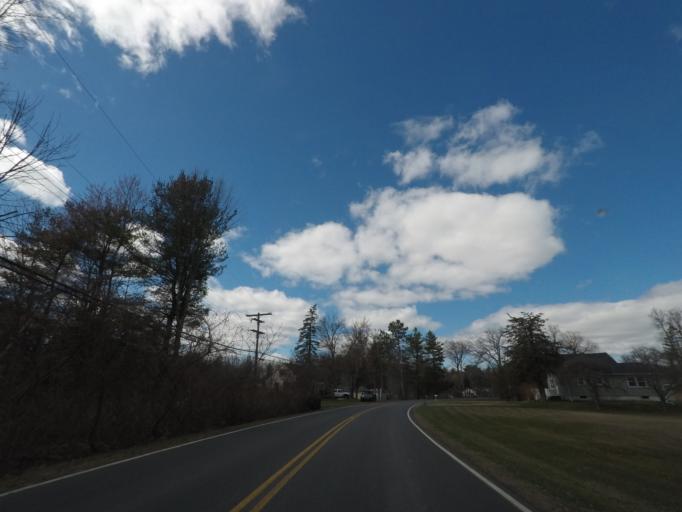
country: US
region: New York
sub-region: Albany County
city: Delmar
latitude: 42.5758
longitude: -73.8294
